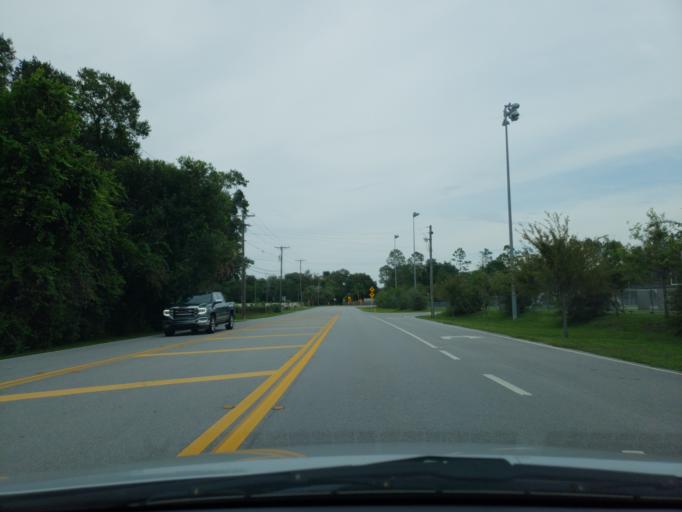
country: US
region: Florida
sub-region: Hillsborough County
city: Lutz
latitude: 28.1539
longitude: -82.4691
